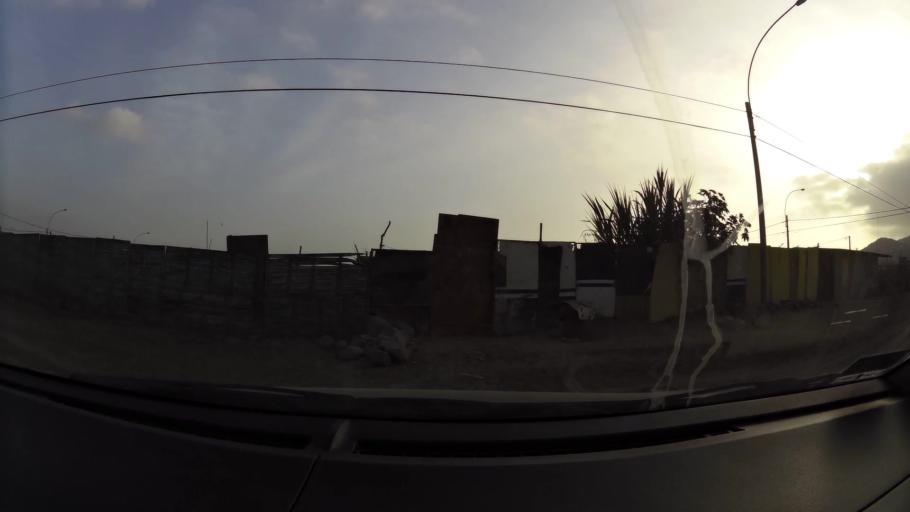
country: PE
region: Lima
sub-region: Lima
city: Santa Rosa
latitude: -11.7405
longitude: -77.1413
